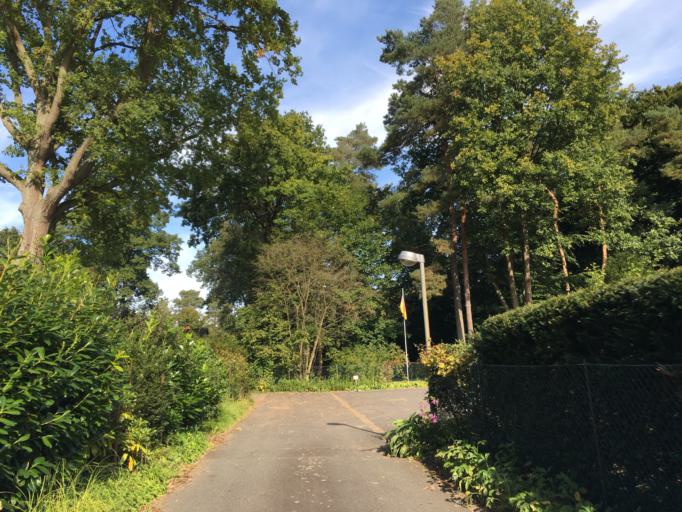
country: DE
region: Lower Saxony
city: Adendorf
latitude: 53.2824
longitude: 10.4647
